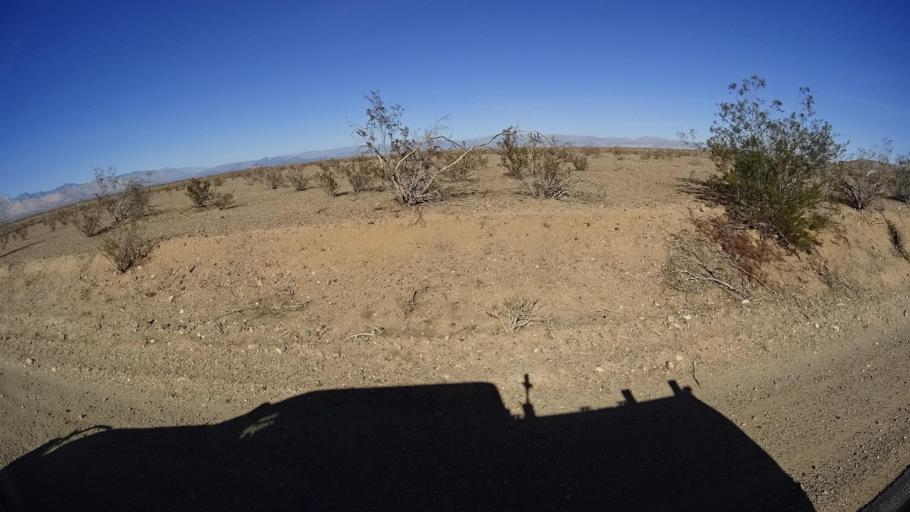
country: US
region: California
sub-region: Kern County
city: China Lake Acres
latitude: 35.5574
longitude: -117.7516
